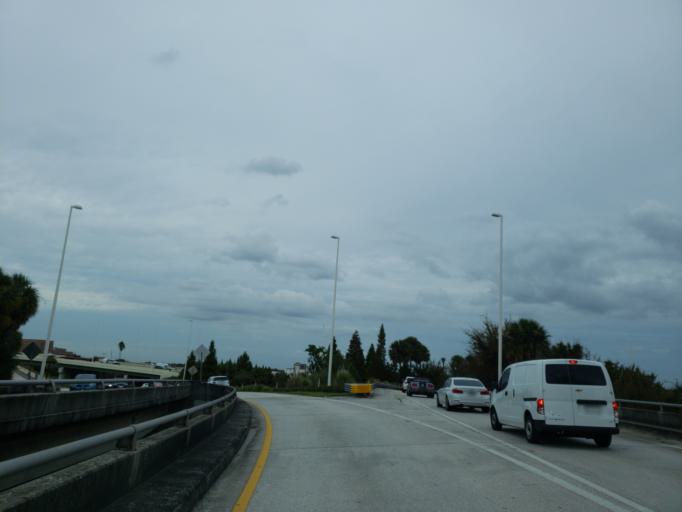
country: US
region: Florida
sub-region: Hillsborough County
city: Tampa
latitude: 27.9549
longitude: -82.4620
